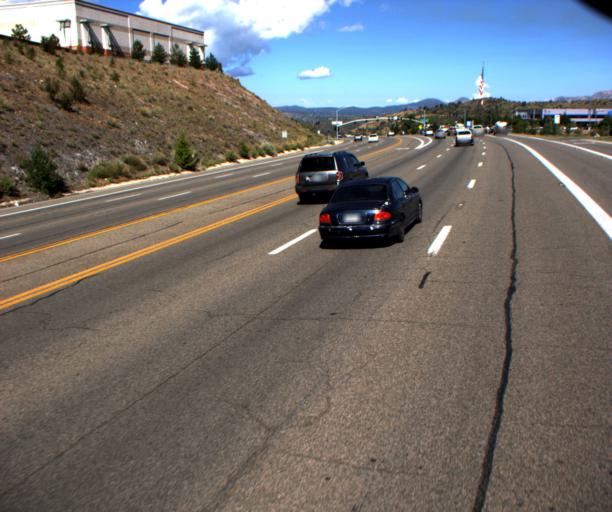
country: US
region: Arizona
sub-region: Yavapai County
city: Prescott
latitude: 34.5512
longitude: -112.4086
